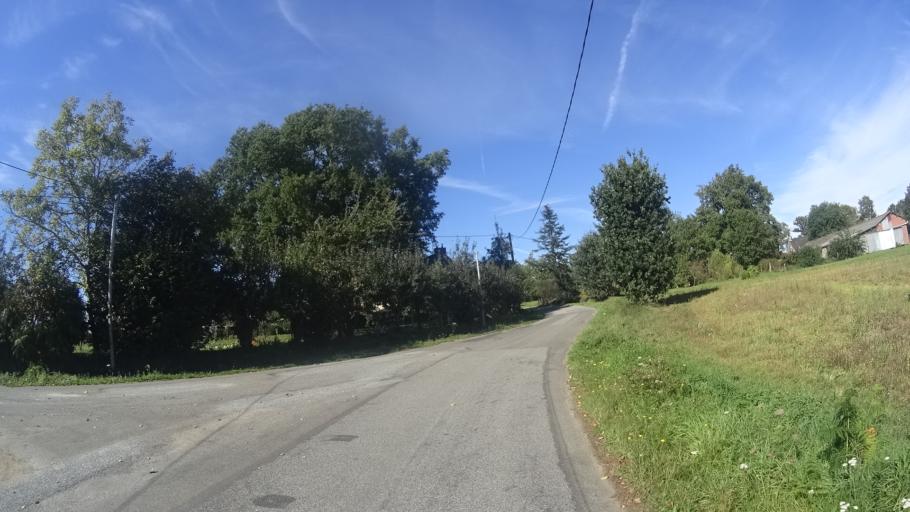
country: FR
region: Brittany
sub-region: Departement du Morbihan
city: Peillac
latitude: 47.7391
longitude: -2.2015
